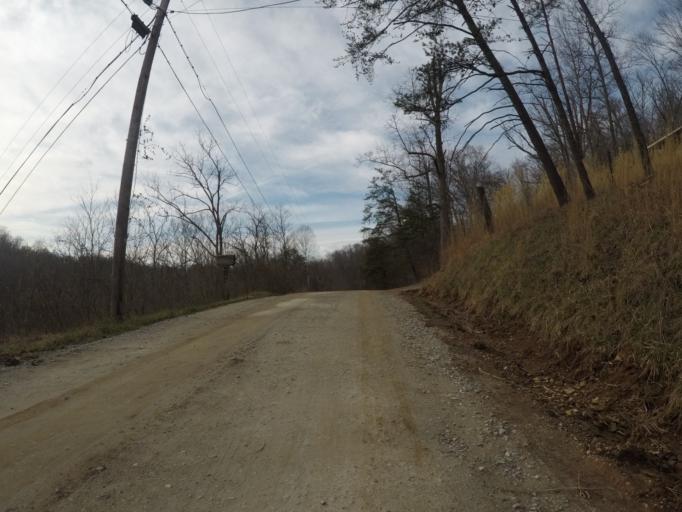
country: US
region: Ohio
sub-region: Lawrence County
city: Burlington
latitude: 38.4602
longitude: -82.5326
